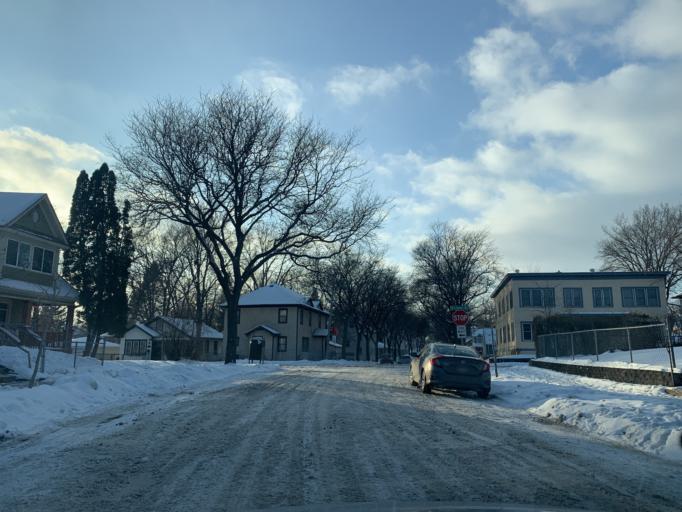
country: US
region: Minnesota
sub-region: Hennepin County
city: Minneapolis
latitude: 44.9862
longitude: -93.3027
